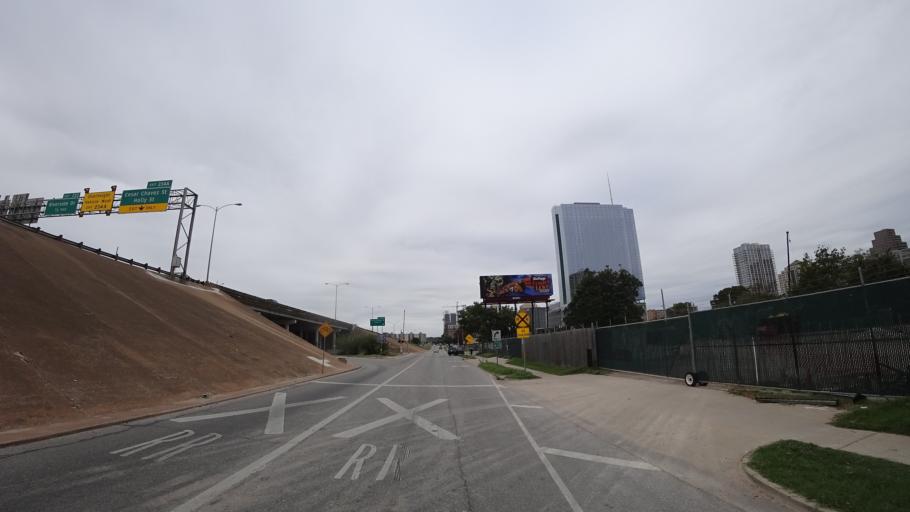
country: US
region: Texas
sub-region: Travis County
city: Austin
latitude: 30.2648
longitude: -97.7355
